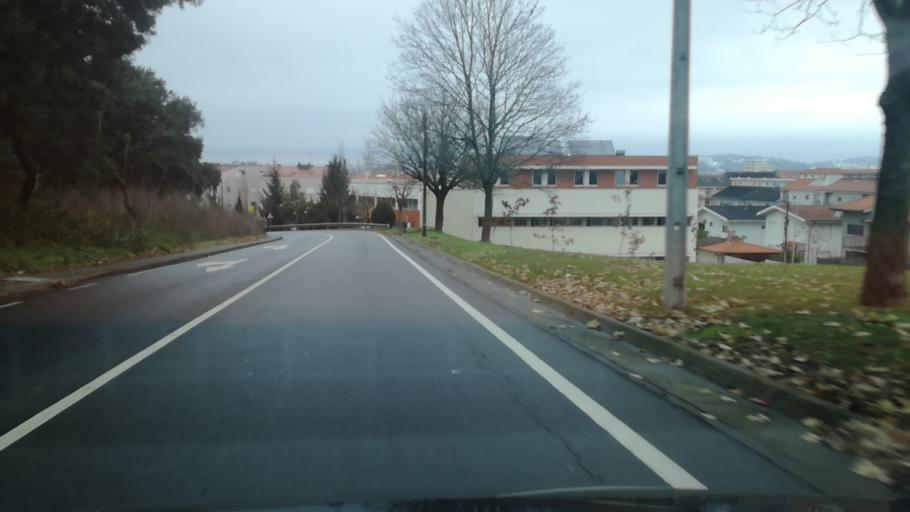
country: PT
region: Braga
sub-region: Braga
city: Braga
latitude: 41.5366
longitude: -8.4100
